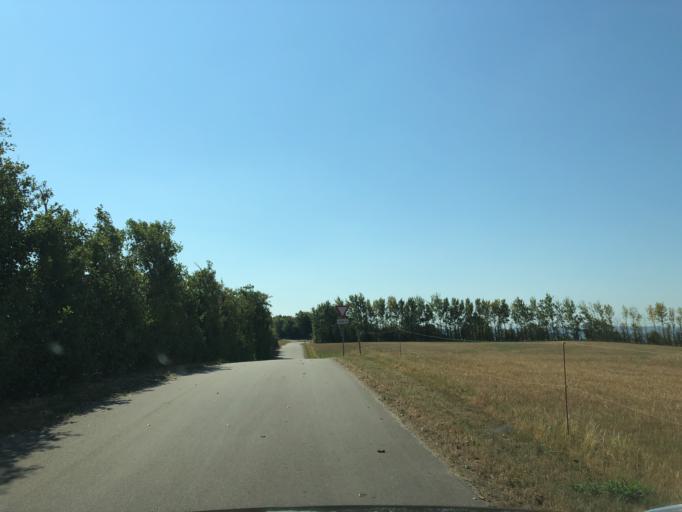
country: DK
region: Zealand
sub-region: Odsherred Kommune
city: Hojby
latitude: 55.9529
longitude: 11.4894
